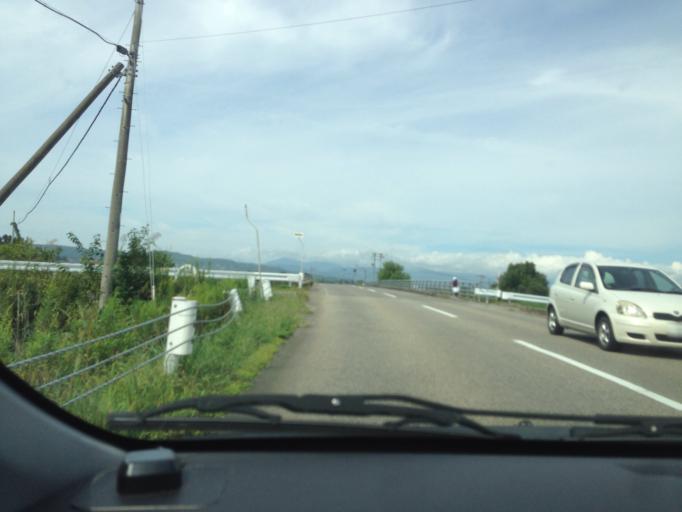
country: JP
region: Fukushima
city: Kitakata
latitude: 37.5485
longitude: 139.8553
